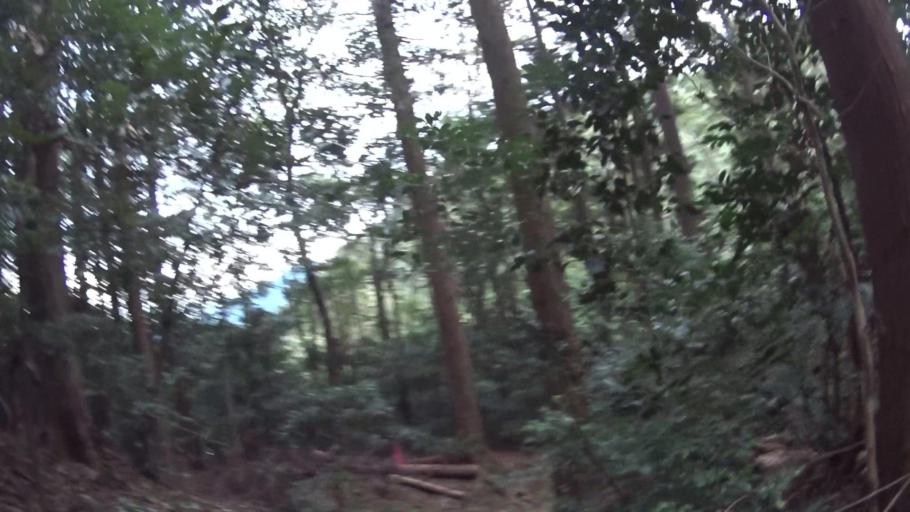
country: JP
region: Osaka
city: Kaizuka
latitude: 34.4697
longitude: 135.3023
